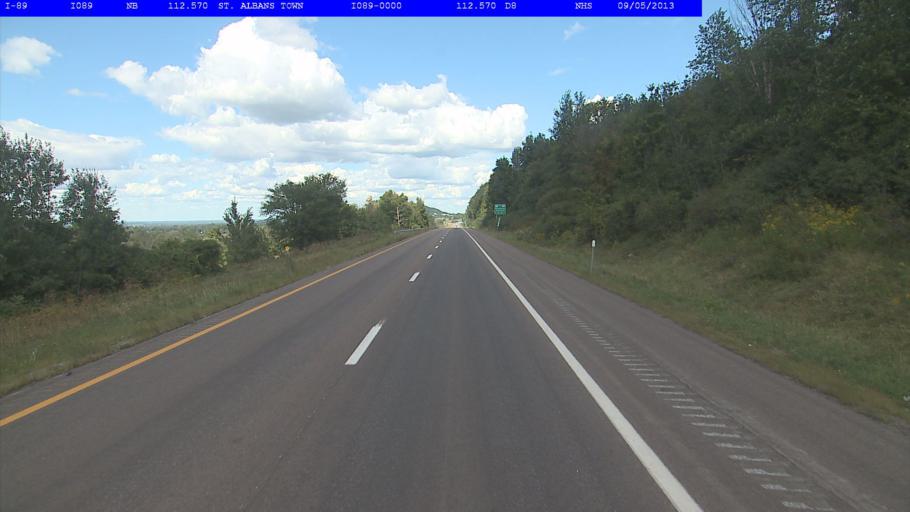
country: US
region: Vermont
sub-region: Franklin County
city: Saint Albans
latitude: 44.7781
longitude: -73.0737
